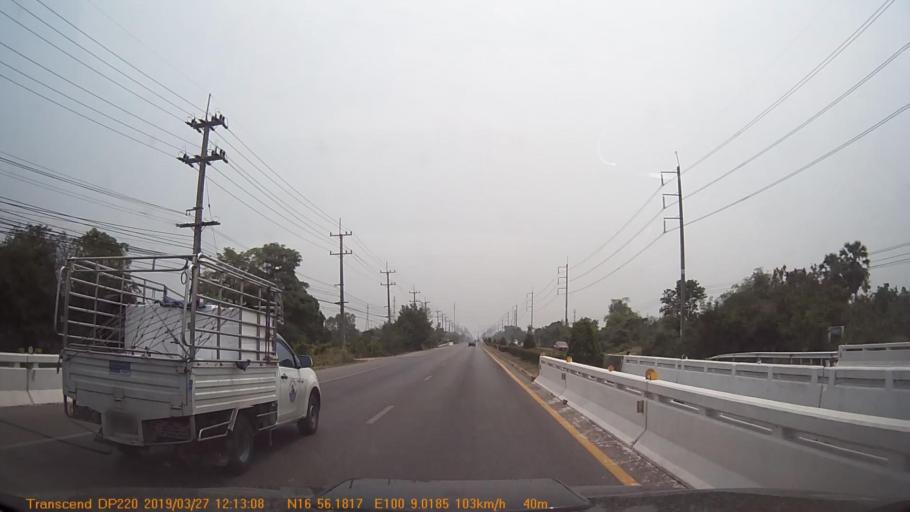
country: TH
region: Phitsanulok
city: Phrom Phiram
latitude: 16.9362
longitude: 100.1506
